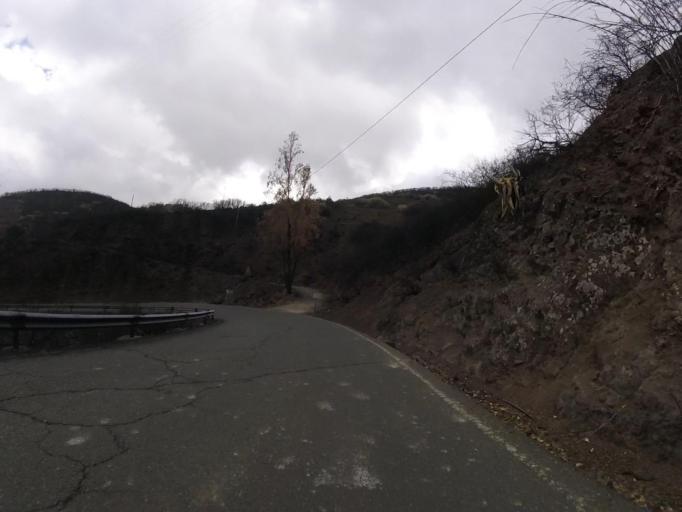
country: ES
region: Canary Islands
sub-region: Provincia de Las Palmas
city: Tejeda
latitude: 27.9839
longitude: -15.5722
